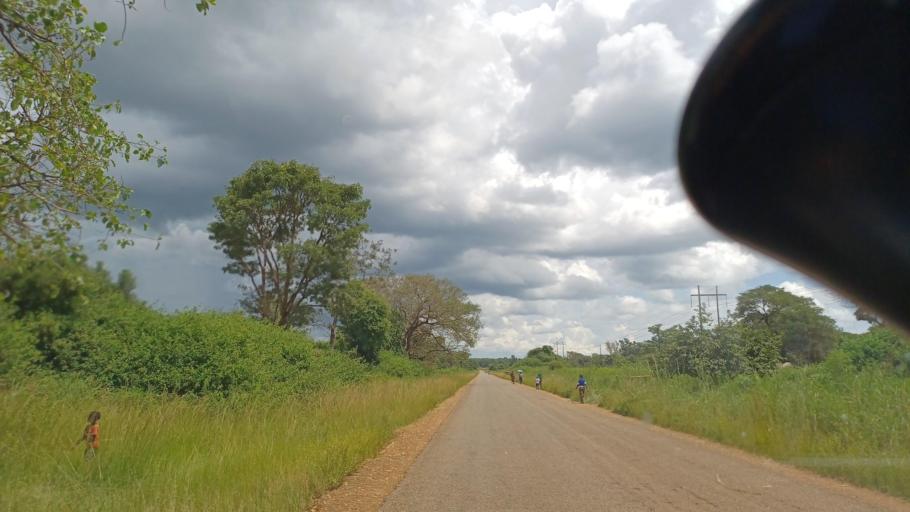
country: ZM
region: North-Western
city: Solwezi
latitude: -12.7713
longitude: 26.0144
